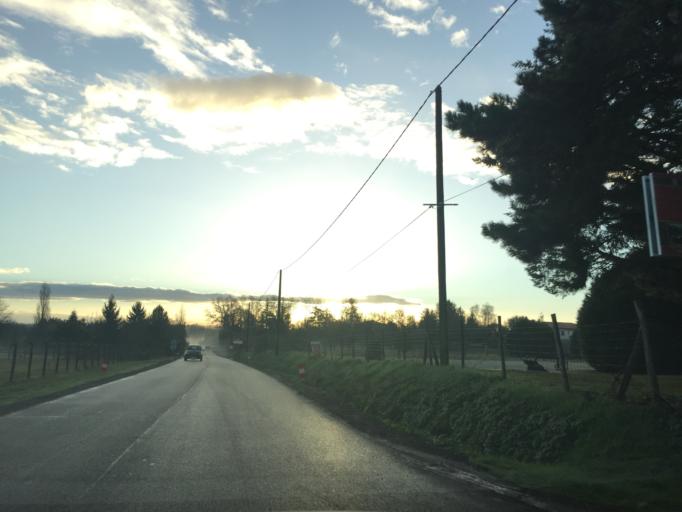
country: FR
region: Aquitaine
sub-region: Departement de la Dordogne
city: Saint-Aulaye
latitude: 45.2760
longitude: 0.1443
